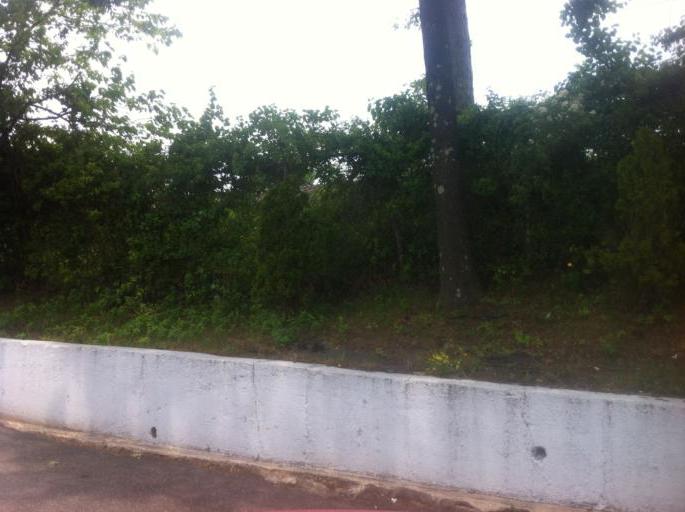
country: US
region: New York
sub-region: Nassau County
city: Massapequa
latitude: 40.6763
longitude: -73.4746
